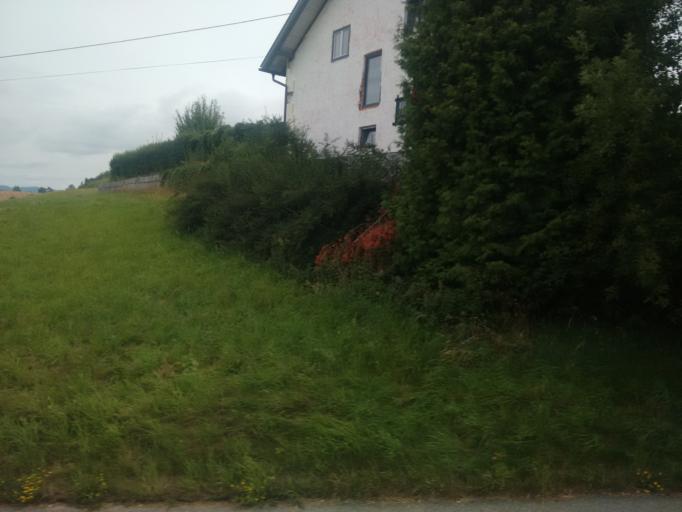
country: AT
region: Upper Austria
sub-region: Politischer Bezirk Ried im Innkreis
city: Ried im Innkreis
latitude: 48.2082
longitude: 13.4263
